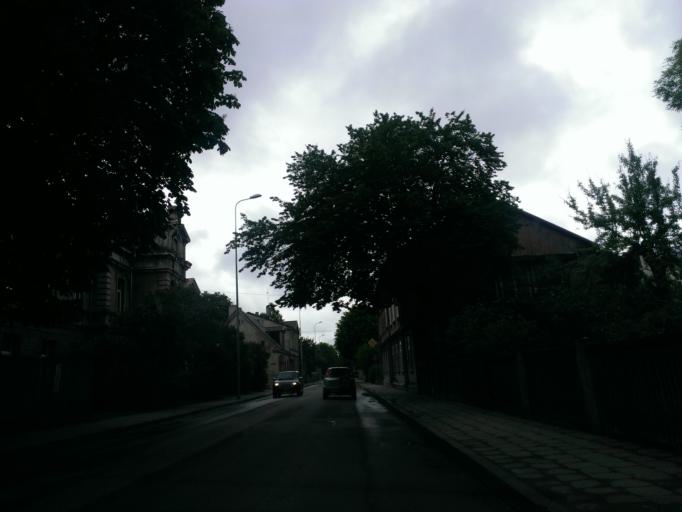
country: LV
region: Liepaja
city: Liepaja
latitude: 56.5055
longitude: 21.0014
